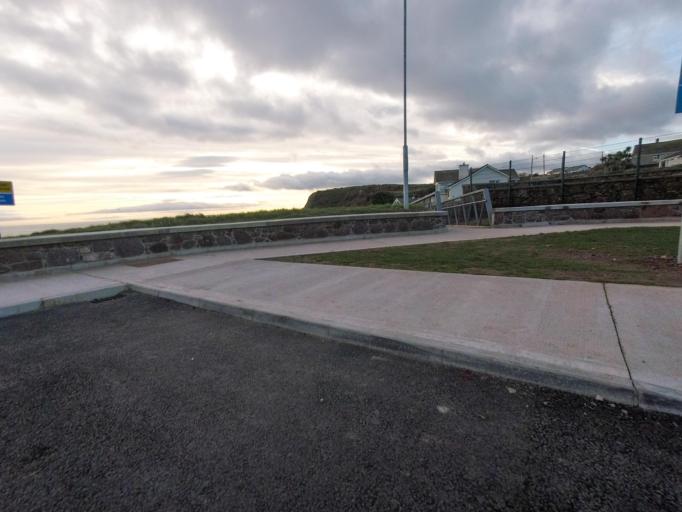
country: IE
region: Munster
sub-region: Waterford
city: Dunmore East
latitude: 52.1452
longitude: -6.9932
